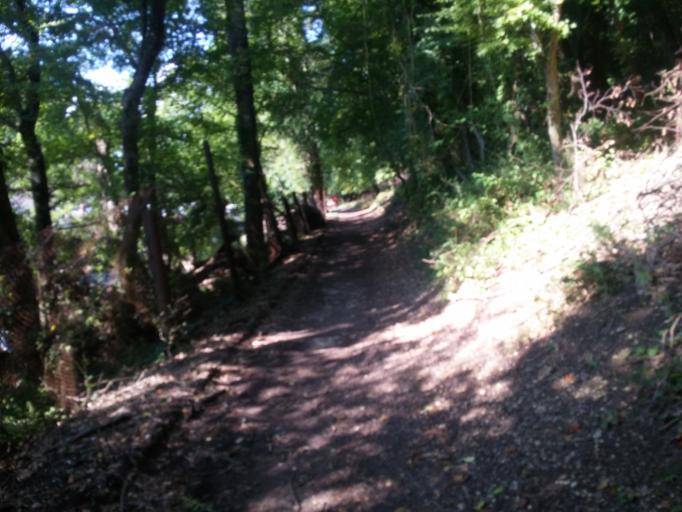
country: RU
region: Krasnodarskiy
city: Divnomorskoye
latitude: 44.4668
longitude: 38.1629
